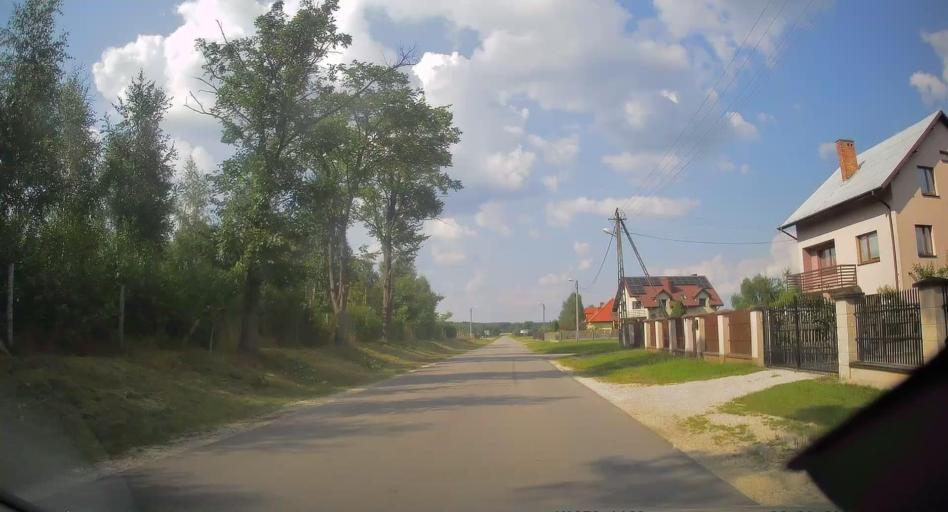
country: PL
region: Swietokrzyskie
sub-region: Powiat konecki
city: Radoszyce
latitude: 51.0838
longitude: 20.2581
